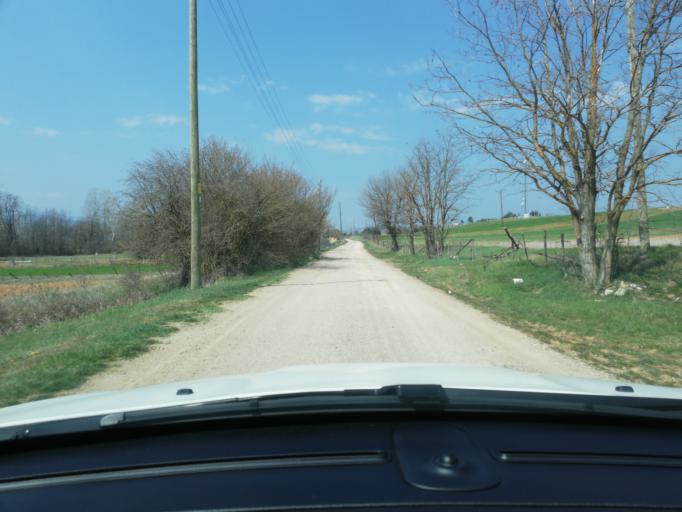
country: TR
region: Kastamonu
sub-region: Cide
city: Kastamonu
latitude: 41.4608
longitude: 33.7524
